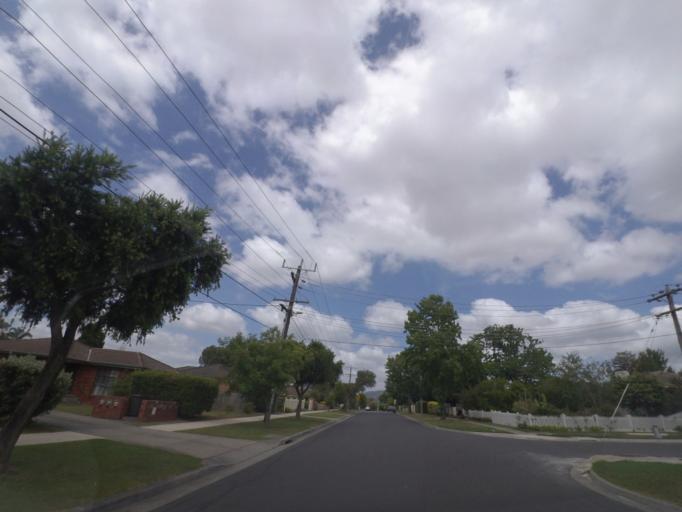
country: AU
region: Victoria
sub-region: Maroondah
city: Croydon South
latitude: -37.8047
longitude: 145.2859
